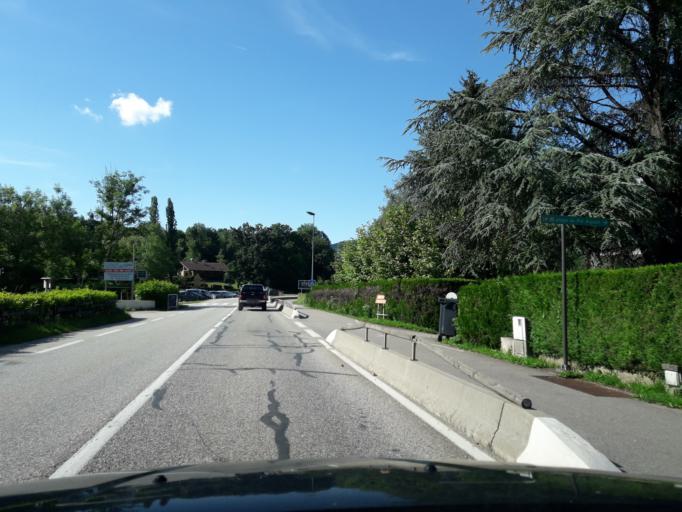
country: FR
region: Rhone-Alpes
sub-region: Departement de la Savoie
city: Novalaise
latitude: 45.5666
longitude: 5.7943
